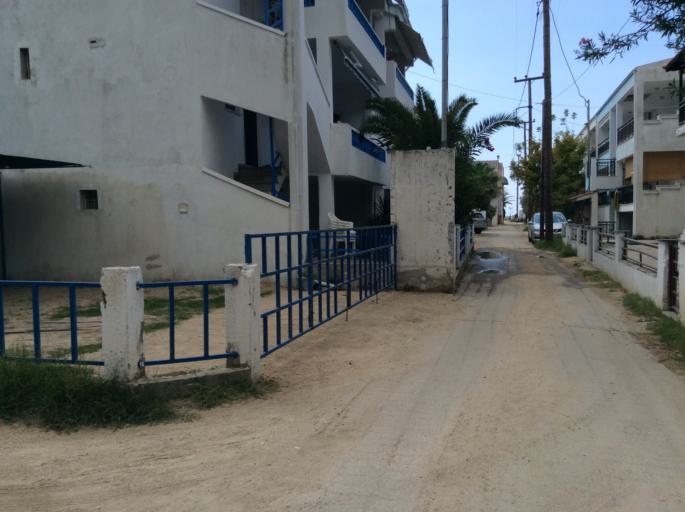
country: GR
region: Central Macedonia
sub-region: Nomos Chalkidikis
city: Sykia
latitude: 39.9893
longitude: 23.9002
